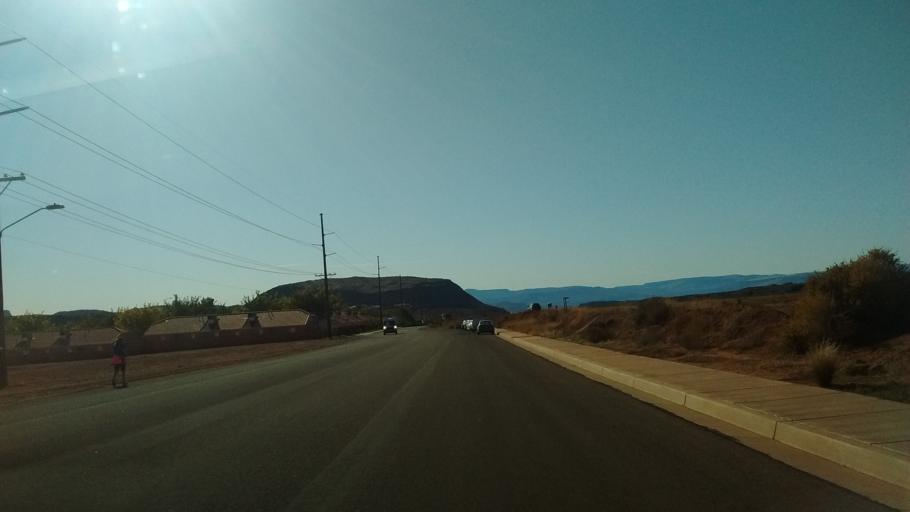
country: US
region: Utah
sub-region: Washington County
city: Washington
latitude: 37.1386
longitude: -113.4912
